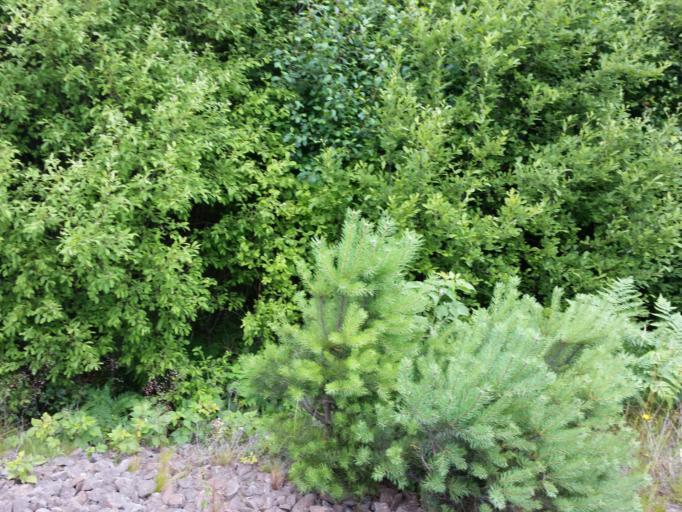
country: SE
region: Kronoberg
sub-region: Almhults Kommun
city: AElmhult
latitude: 56.6105
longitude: 14.1915
